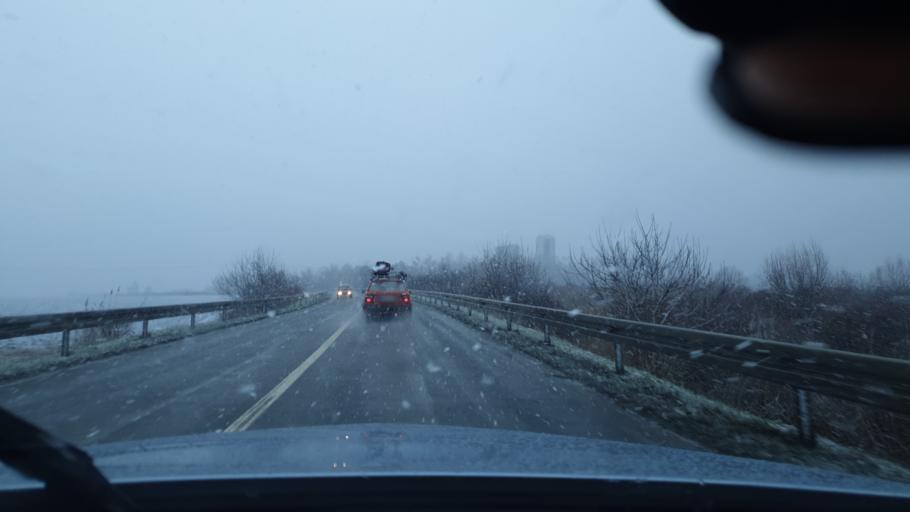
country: RS
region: Autonomna Pokrajina Vojvodina
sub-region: Juznobanatski Okrug
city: Pancevo
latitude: 44.8627
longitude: 20.7398
